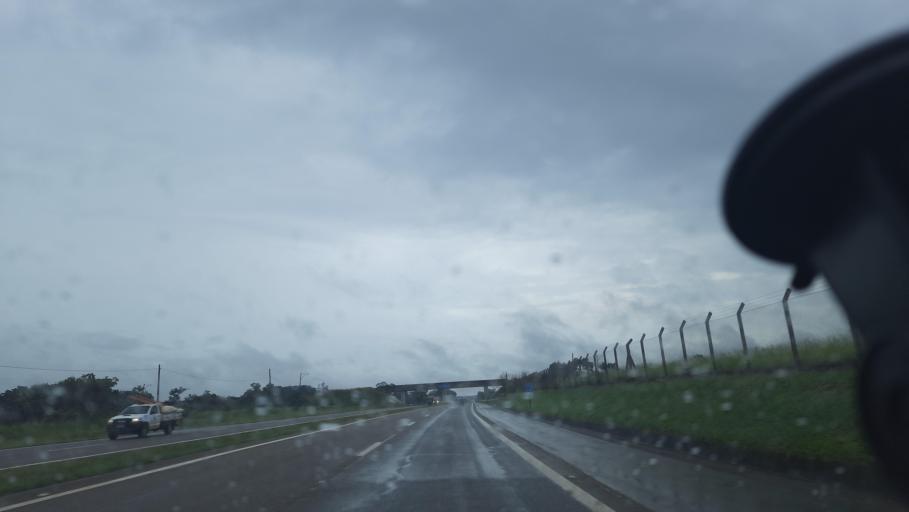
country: BR
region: Sao Paulo
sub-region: Casa Branca
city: Casa Branca
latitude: -21.8048
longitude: -47.0602
